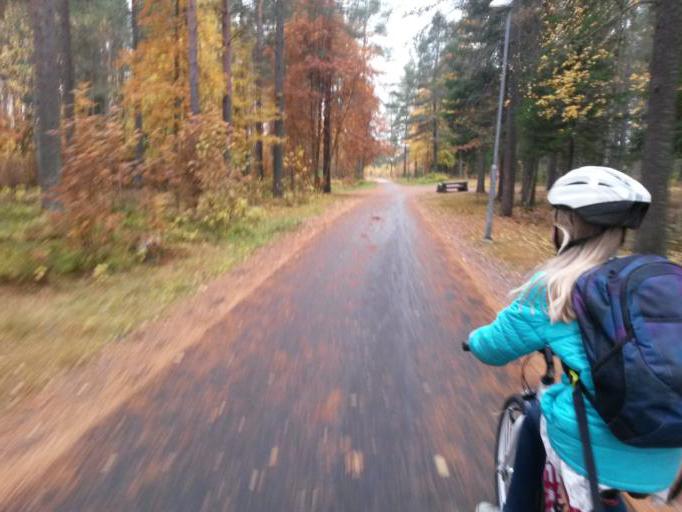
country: SE
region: Vaesterbotten
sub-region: Skelleftea Kommun
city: Skelleftea
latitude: 64.7538
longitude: 21.0215
